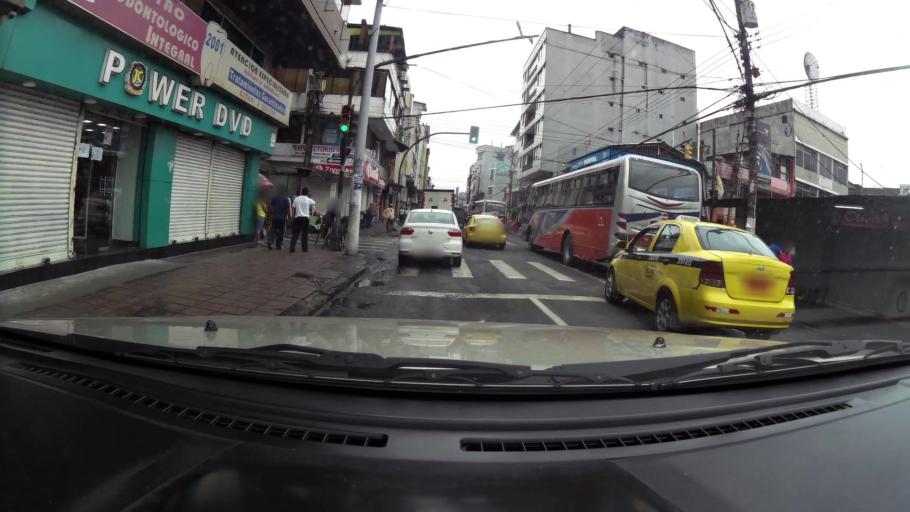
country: EC
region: Santo Domingo de los Tsachilas
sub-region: Canton Santo Domingo de los Colorados
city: Santo Domingo de los Colorados
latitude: -0.2536
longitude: -79.1716
